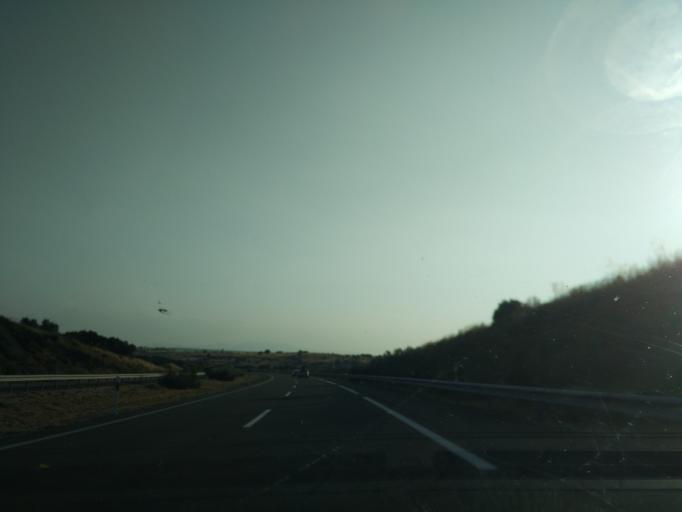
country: ES
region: Castille and Leon
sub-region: Provincia de Avila
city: Mediana de Voltoya
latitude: 40.7126
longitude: -4.5572
